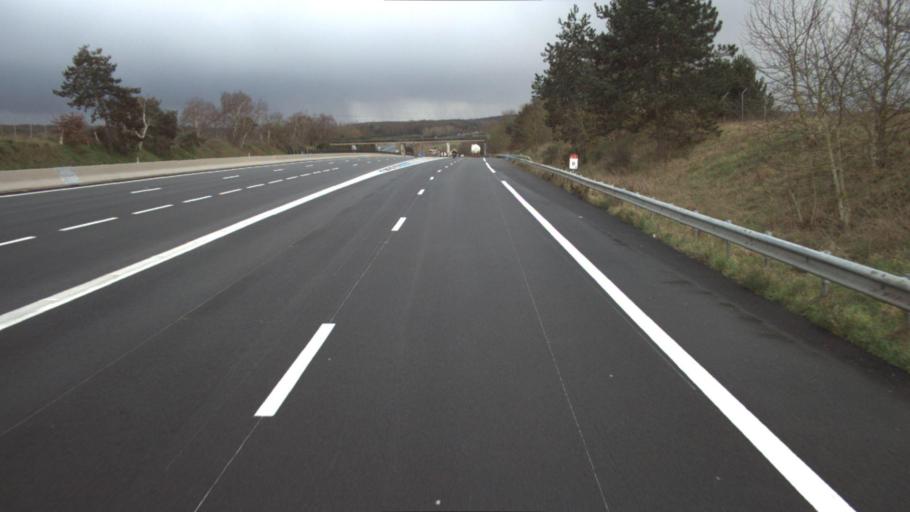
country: FR
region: Ile-de-France
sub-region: Departement de l'Essonne
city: Soisy-sur-Ecole
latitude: 48.4839
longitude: 2.5134
